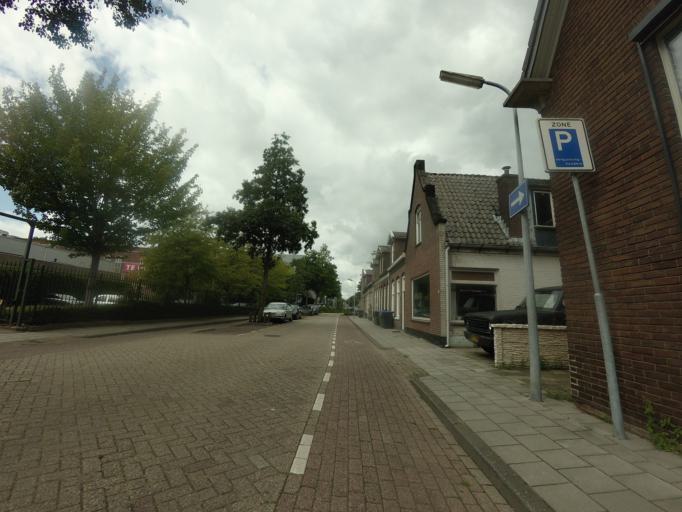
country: NL
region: Drenthe
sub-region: Gemeente Meppel
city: Meppel
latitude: 52.7013
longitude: 6.1863
